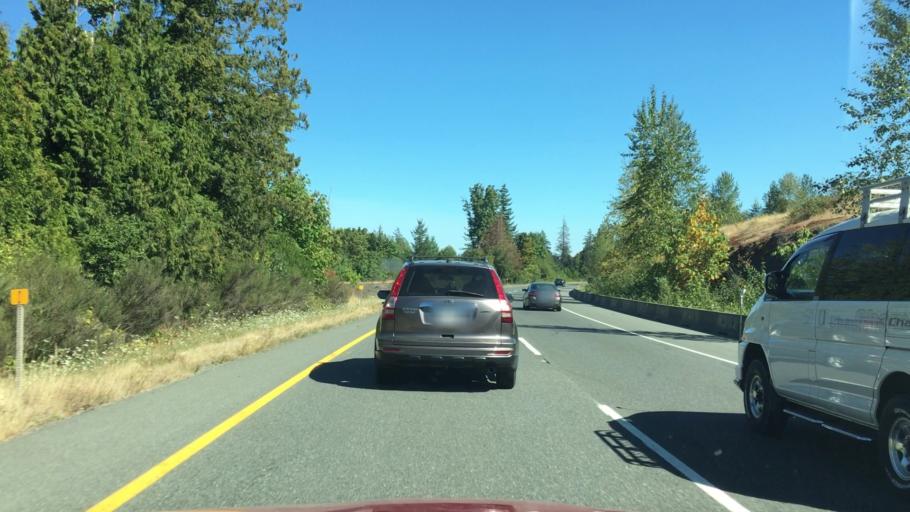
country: CA
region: British Columbia
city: Nanaimo
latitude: 49.1345
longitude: -123.9355
